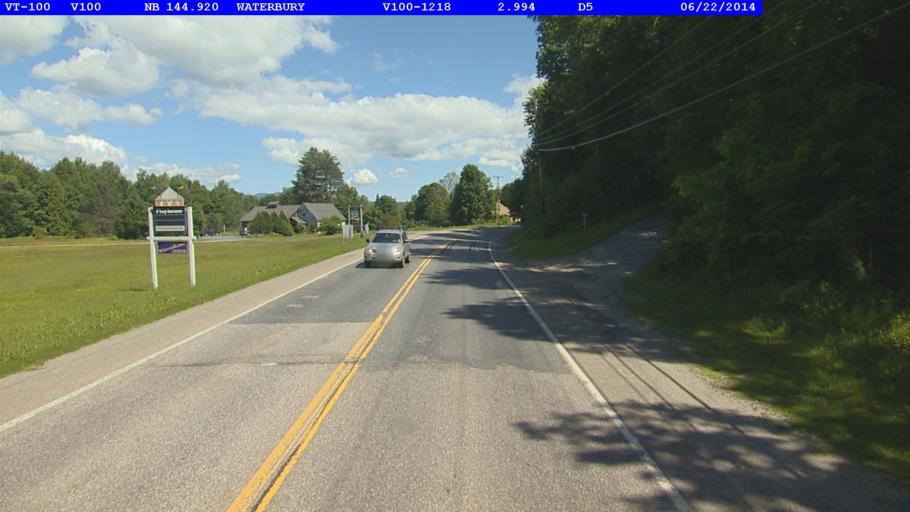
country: US
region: Vermont
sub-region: Washington County
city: Waterbury
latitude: 44.3738
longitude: -72.7263
